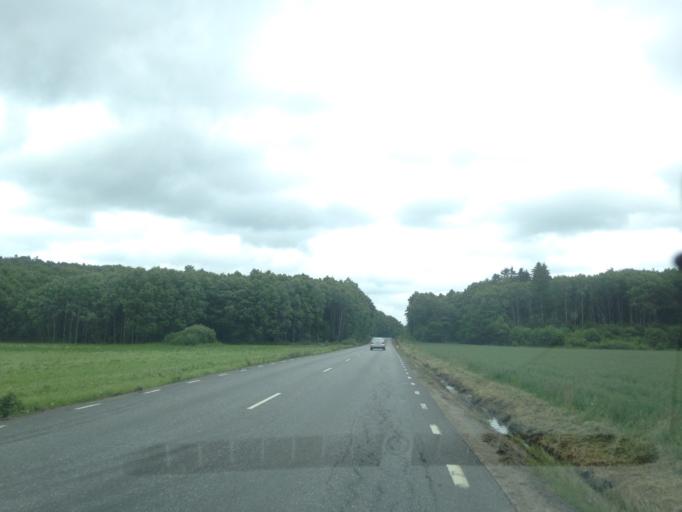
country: SE
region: Vaestra Goetaland
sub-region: Kungalvs Kommun
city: Kode
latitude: 57.8573
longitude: 11.8490
